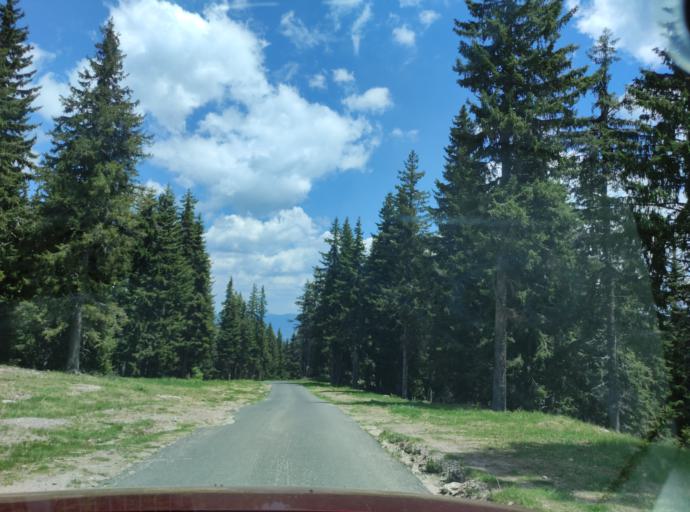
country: BG
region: Smolyan
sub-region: Obshtina Smolyan
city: Smolyan
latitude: 41.6368
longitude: 24.6830
